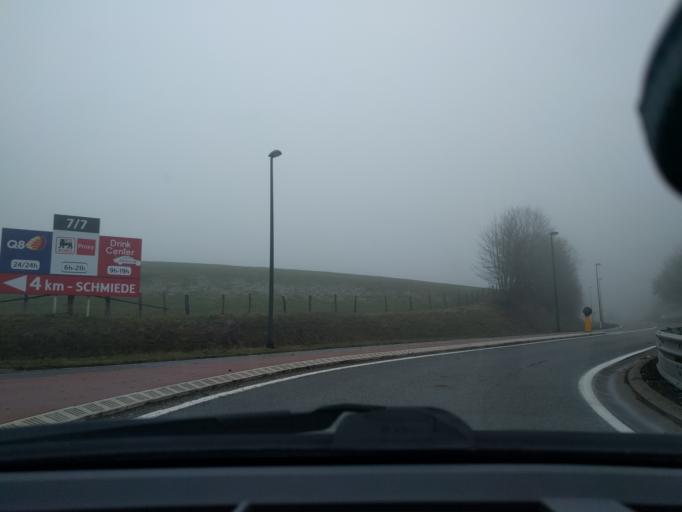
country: BE
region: Wallonia
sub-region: Province du Luxembourg
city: Gouvy
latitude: 50.2135
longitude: 5.9872
